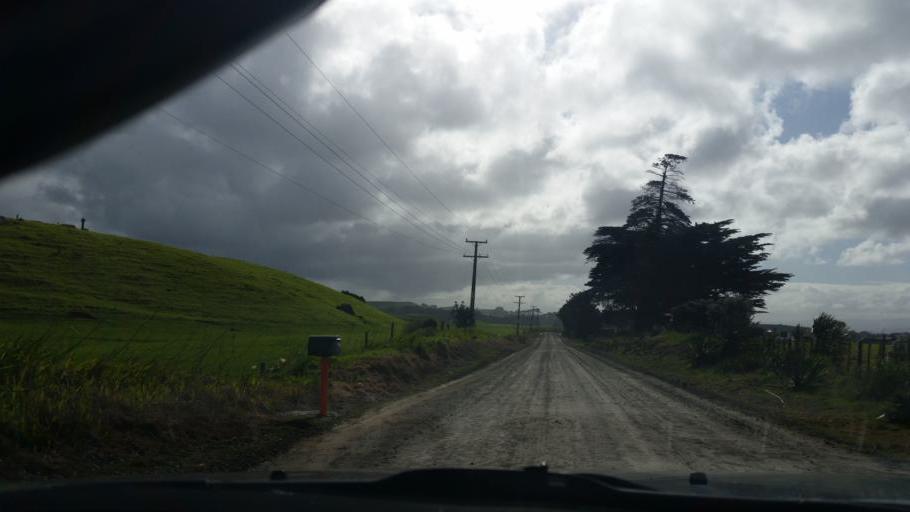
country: NZ
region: Northland
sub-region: Kaipara District
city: Dargaville
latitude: -36.0597
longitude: 173.8748
